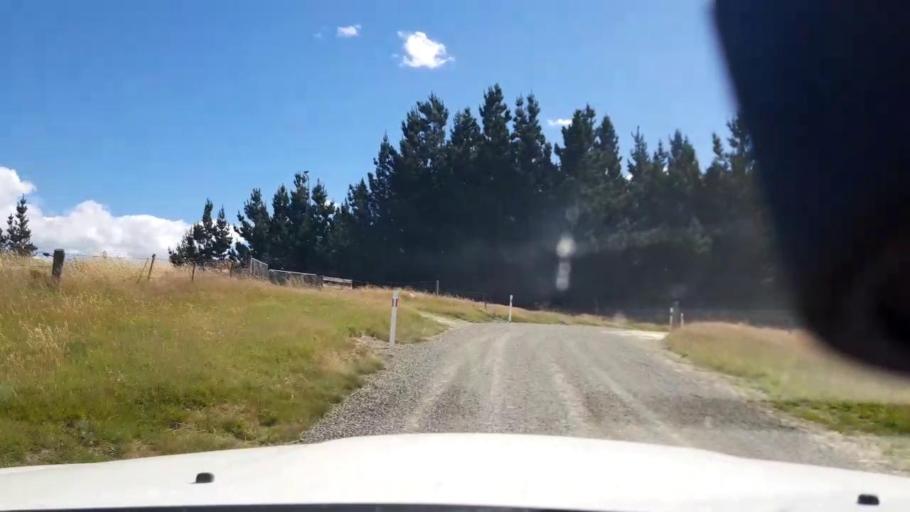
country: NZ
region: Canterbury
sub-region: Timaru District
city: Pleasant Point
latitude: -44.3207
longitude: 170.8795
